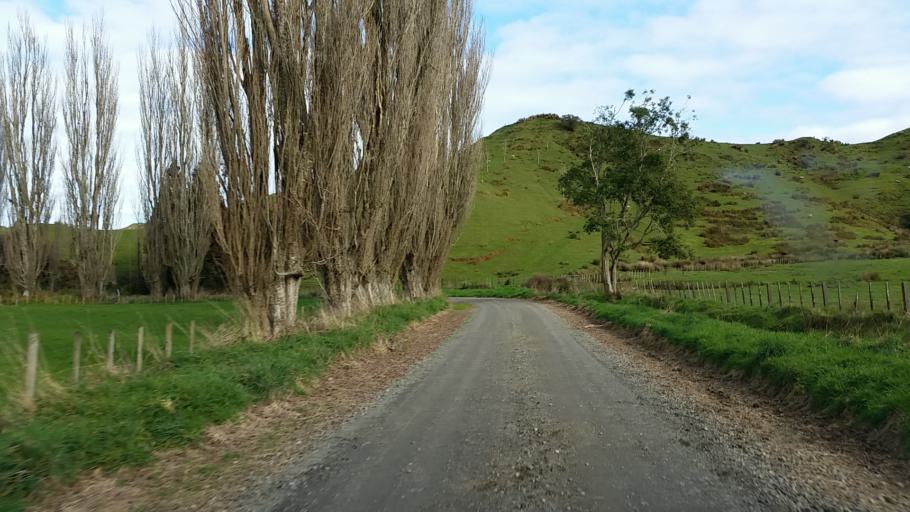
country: NZ
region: Taranaki
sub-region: South Taranaki District
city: Eltham
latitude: -39.2542
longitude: 174.5304
